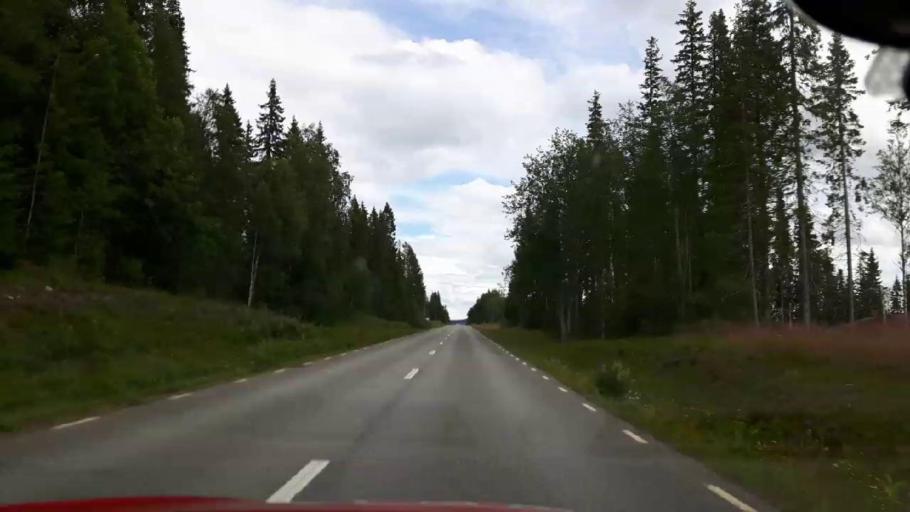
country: NO
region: Nord-Trondelag
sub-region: Lierne
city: Sandvika
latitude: 64.3900
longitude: 14.4387
